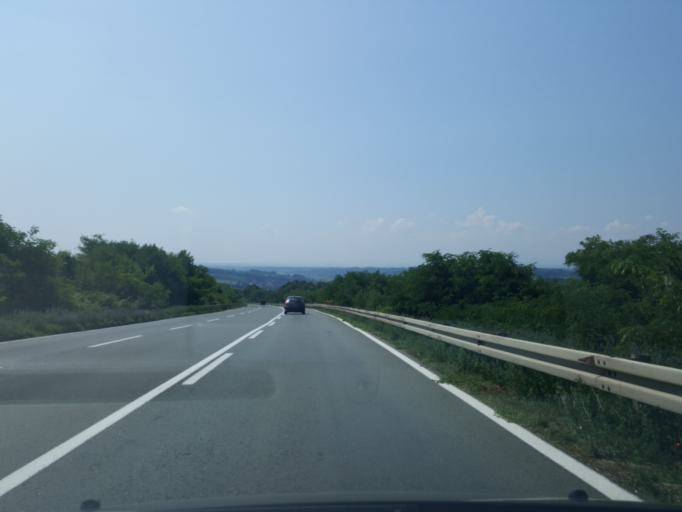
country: RS
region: Central Serbia
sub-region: Belgrade
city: Sopot
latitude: 44.5135
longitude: 20.6530
